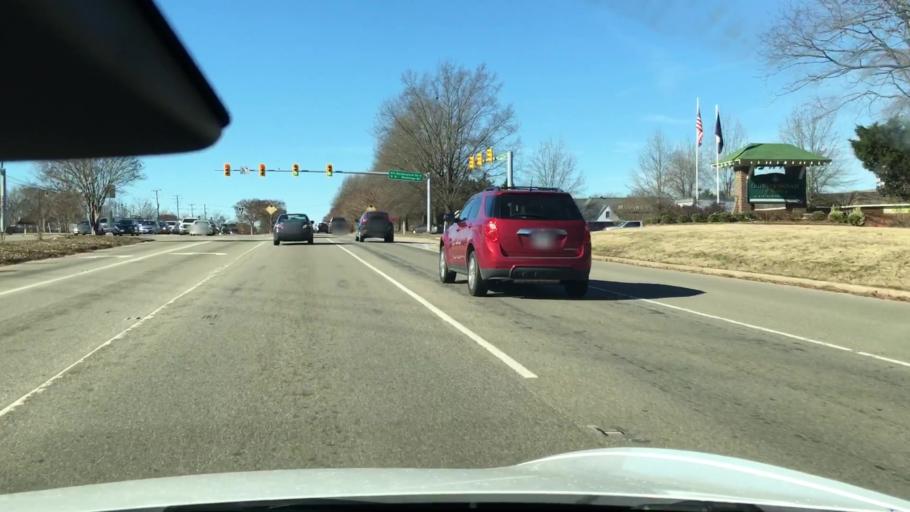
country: US
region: Virginia
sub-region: Chesterfield County
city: Brandermill
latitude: 37.5027
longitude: -77.6397
